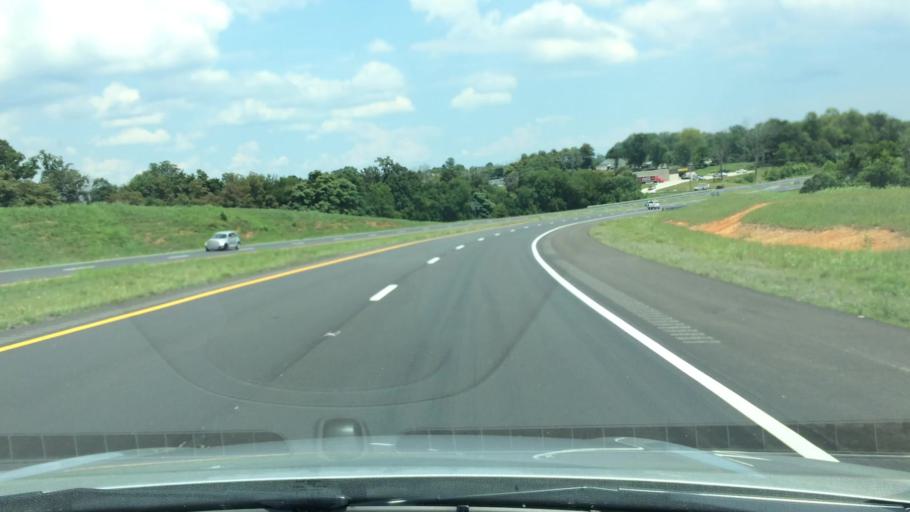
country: US
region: Tennessee
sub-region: Hamblen County
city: Morristown
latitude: 36.1826
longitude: -83.2387
